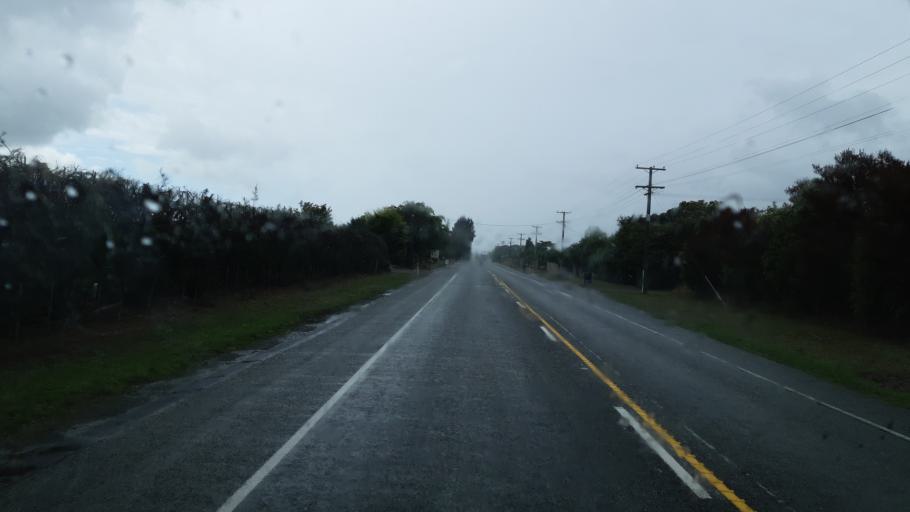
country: NZ
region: Tasman
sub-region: Tasman District
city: Brightwater
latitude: -41.3693
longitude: 173.1296
